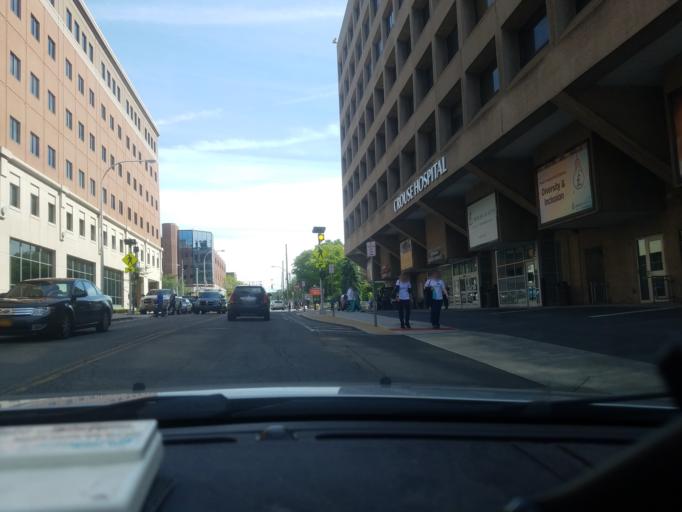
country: US
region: New York
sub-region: Onondaga County
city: Syracuse
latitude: 43.0417
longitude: -76.1379
